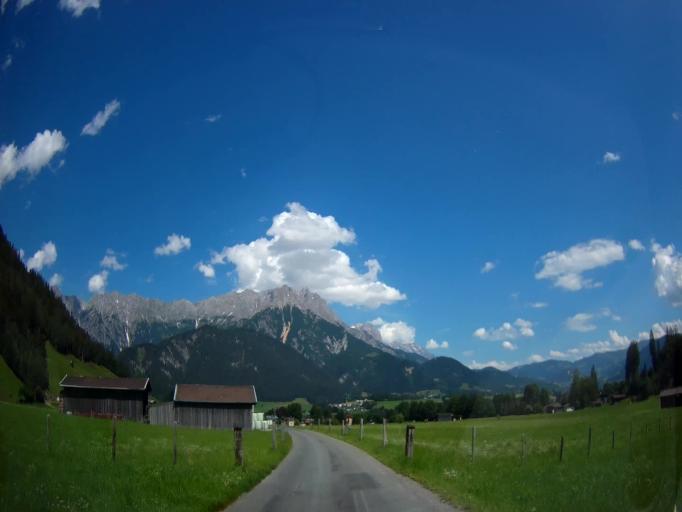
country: AT
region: Salzburg
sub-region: Politischer Bezirk Zell am See
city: Leogang
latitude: 47.4498
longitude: 12.8009
